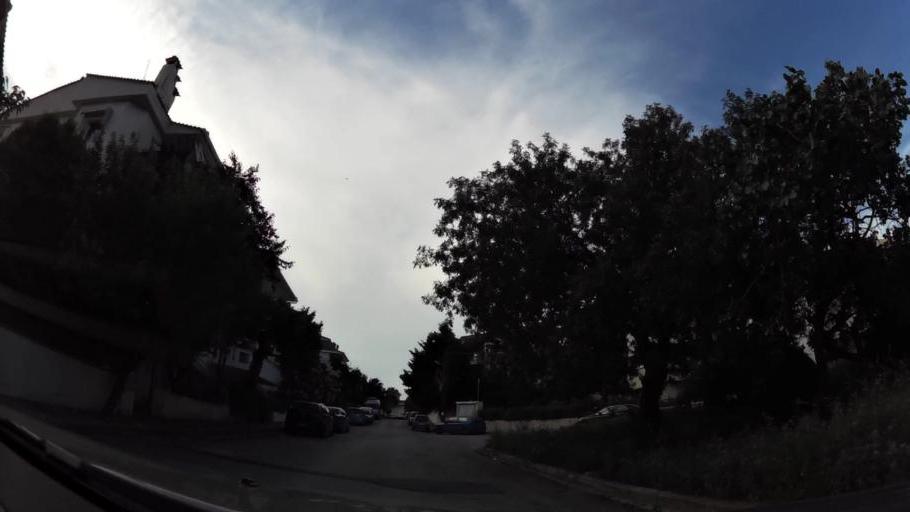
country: GR
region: Central Macedonia
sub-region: Nomos Thessalonikis
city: Pefka
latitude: 40.6522
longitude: 22.9996
